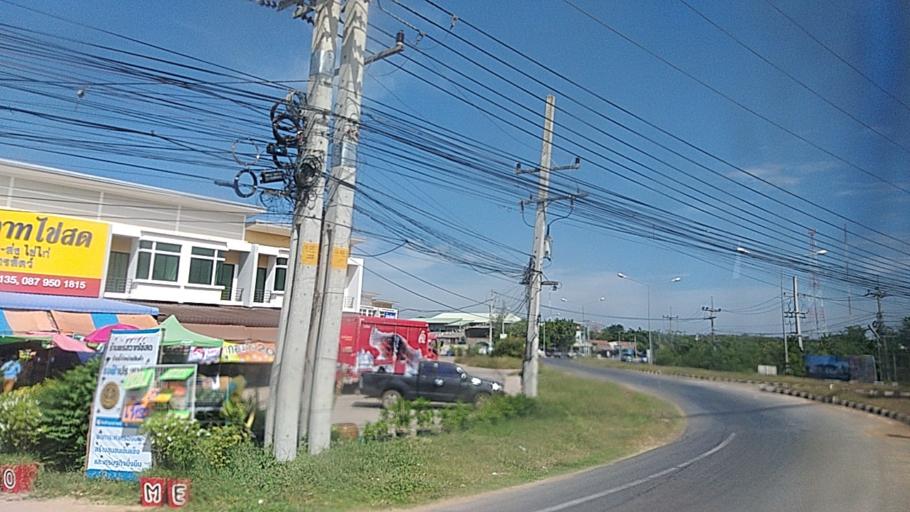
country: TH
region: Khon Kaen
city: Khon Kaen
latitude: 16.4453
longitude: 102.9475
